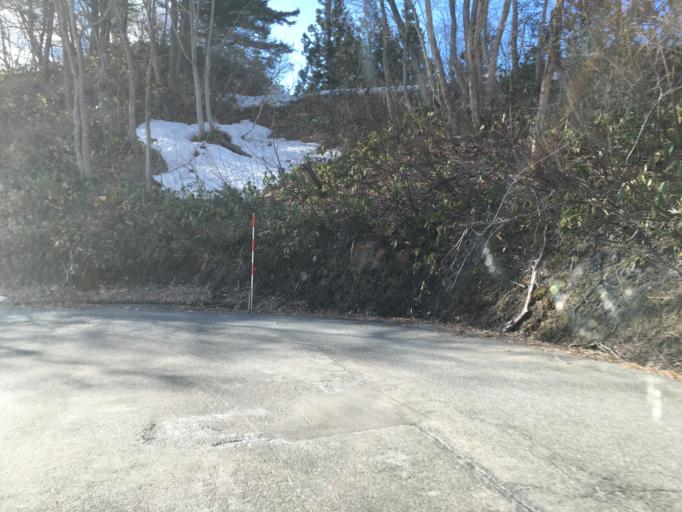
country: JP
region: Yamagata
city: Yonezawa
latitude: 37.9249
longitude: 139.9408
